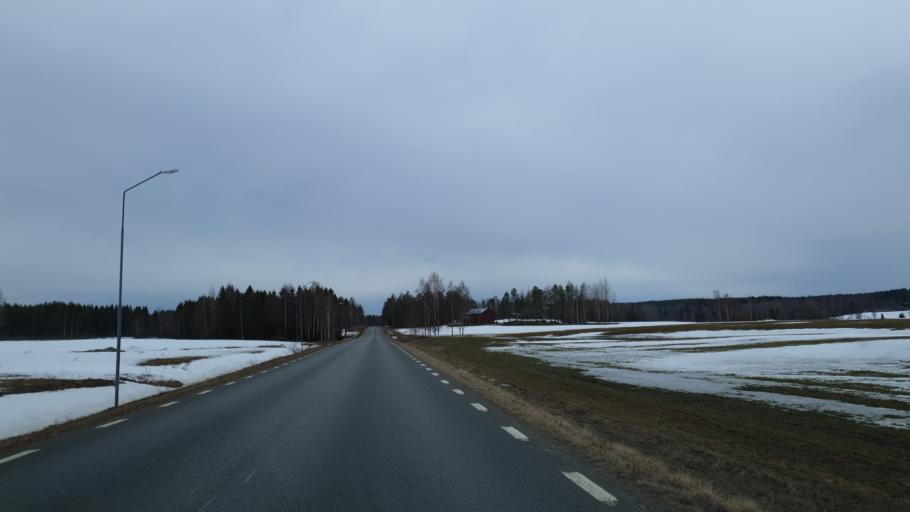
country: SE
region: Vaesterbotten
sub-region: Robertsfors Kommun
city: Robertsfors
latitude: 64.3825
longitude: 20.8981
